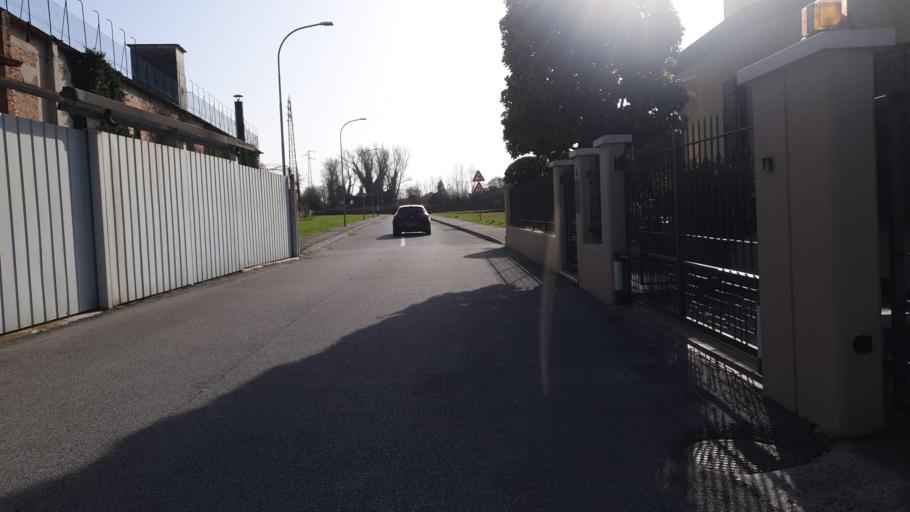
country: IT
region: Veneto
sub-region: Provincia di Padova
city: Vigodarzere
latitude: 45.4514
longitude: 11.8877
